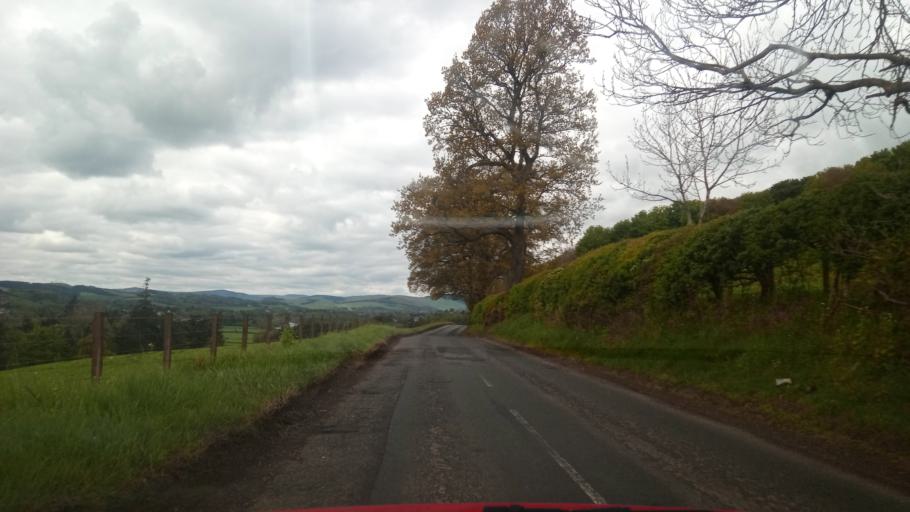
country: GB
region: Scotland
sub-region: The Scottish Borders
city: Newtown St Boswells
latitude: 55.6056
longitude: -2.6885
